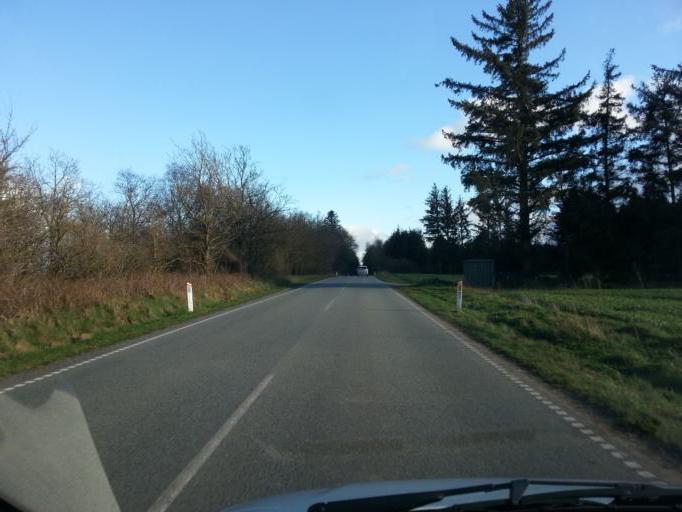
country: DK
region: South Denmark
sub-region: Varde Kommune
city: Olgod
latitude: 55.8396
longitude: 8.5608
